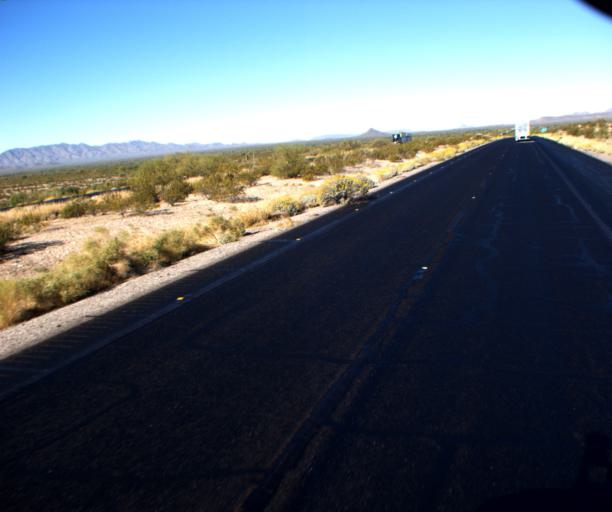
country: US
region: Arizona
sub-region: Pinal County
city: Maricopa
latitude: 32.8386
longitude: -112.2246
